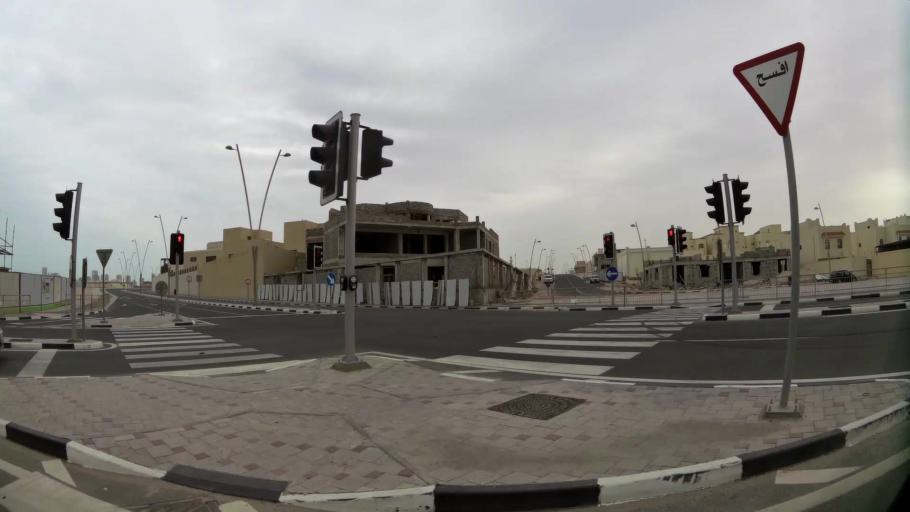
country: QA
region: Baladiyat ad Dawhah
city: Doha
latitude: 25.3439
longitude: 51.4921
